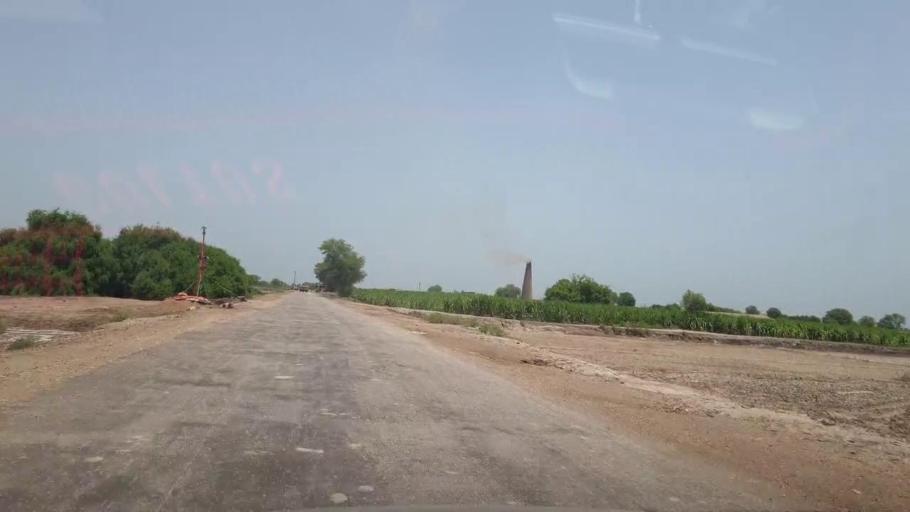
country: PK
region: Sindh
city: Daulatpur
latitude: 26.3894
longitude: 68.0869
